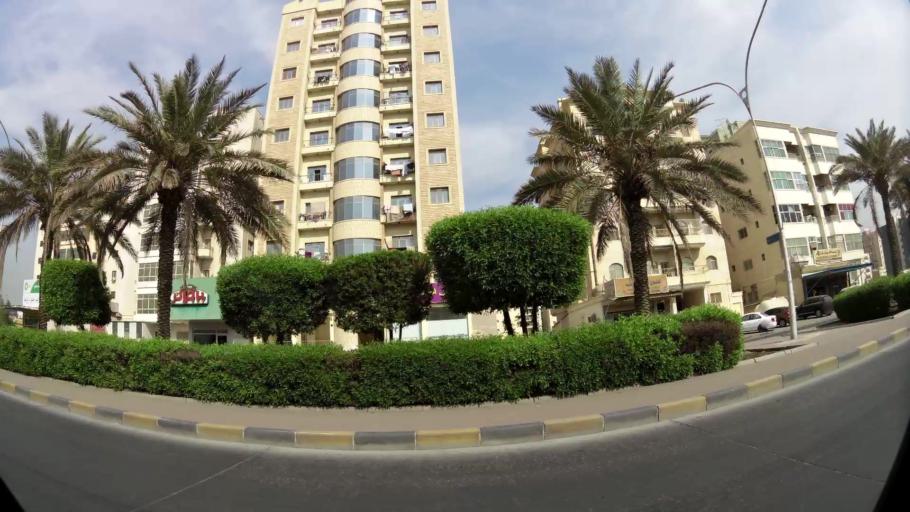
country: KW
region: Al Farwaniyah
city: Al Farwaniyah
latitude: 29.2824
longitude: 47.9697
